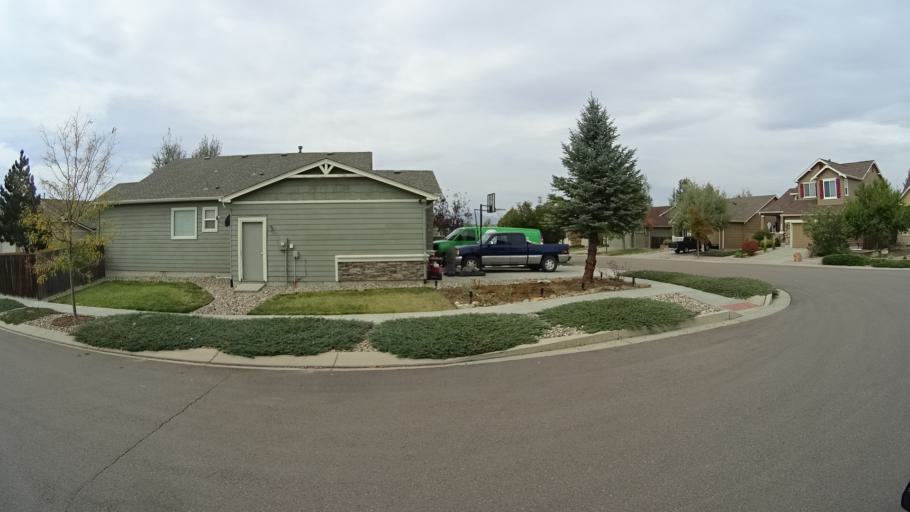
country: US
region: Colorado
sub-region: El Paso County
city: Cimarron Hills
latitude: 38.9205
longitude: -104.6864
